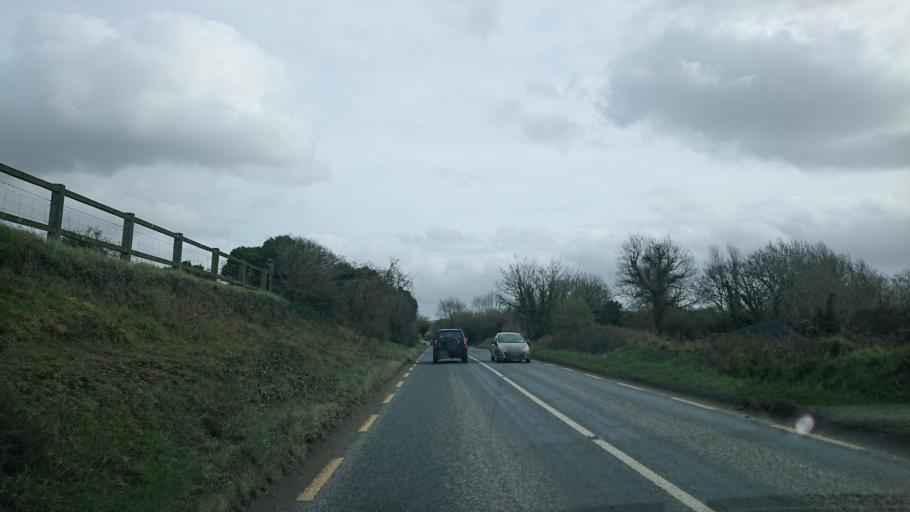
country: IE
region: Leinster
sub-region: Kildare
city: Johnstown
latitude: 53.2020
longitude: -6.6230
